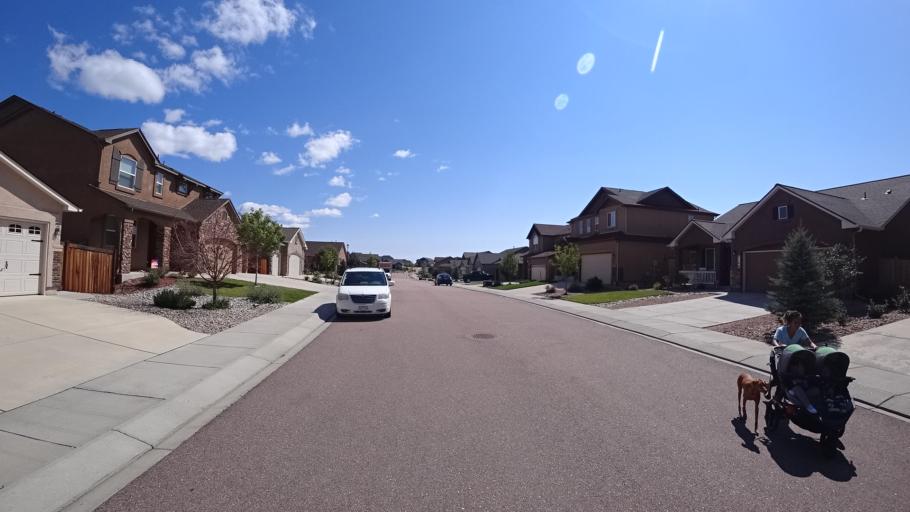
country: US
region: Colorado
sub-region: El Paso County
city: Cimarron Hills
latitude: 38.9291
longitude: -104.6872
